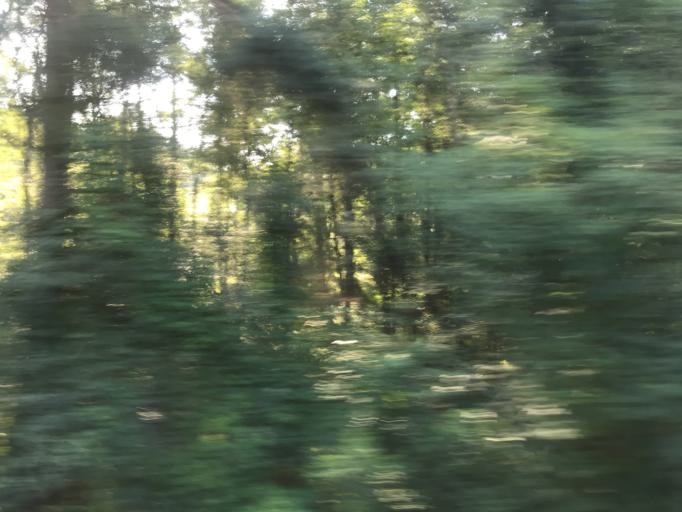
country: CZ
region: Jihocesky
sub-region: Okres Jindrichuv Hradec
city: Lomnice nad Luznici
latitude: 49.1219
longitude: 14.7375
